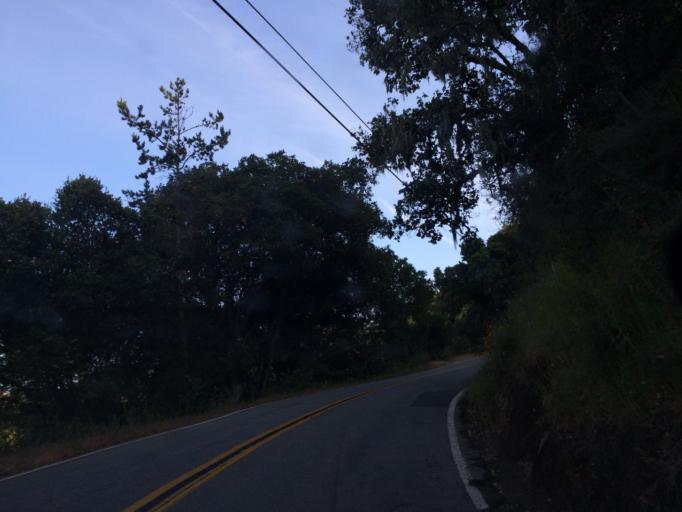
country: US
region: California
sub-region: Santa Clara County
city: Los Altos Hills
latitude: 37.3622
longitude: -122.1704
